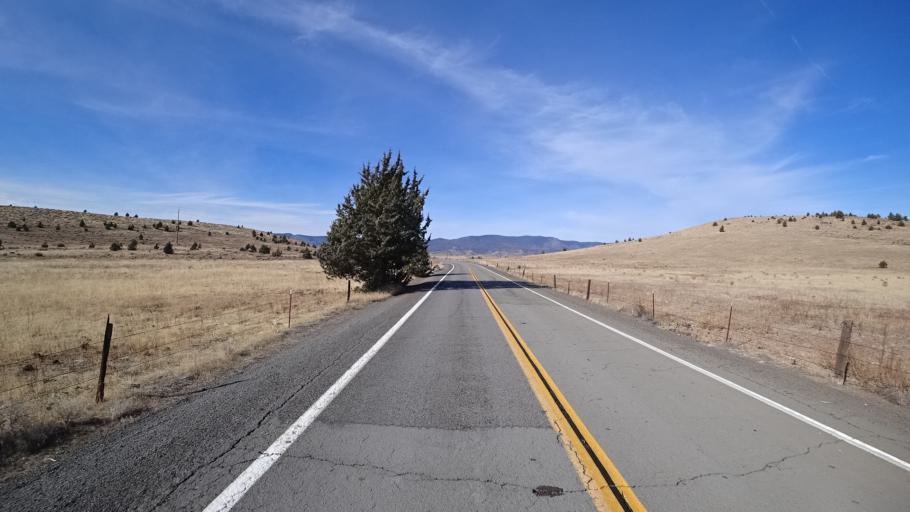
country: US
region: California
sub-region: Siskiyou County
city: Weed
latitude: 41.5539
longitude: -122.4787
